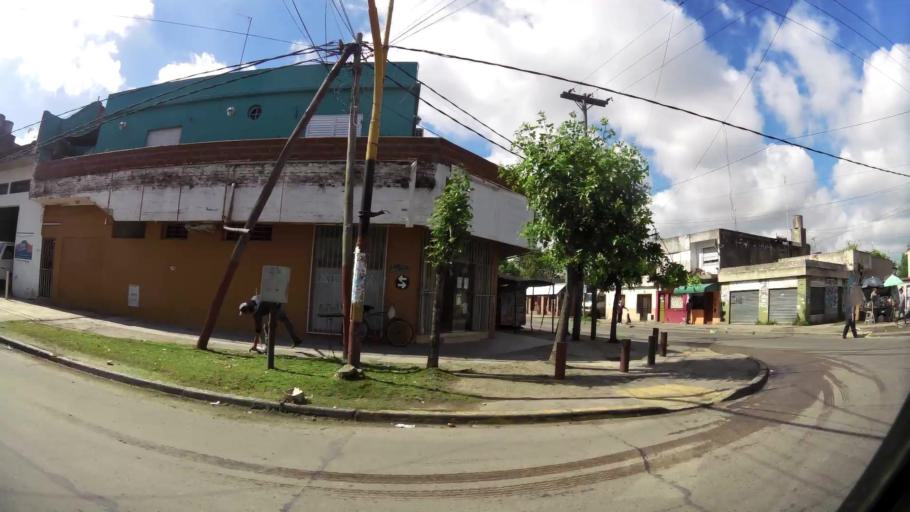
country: AR
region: Buenos Aires F.D.
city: Villa Lugano
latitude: -34.6797
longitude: -58.4311
